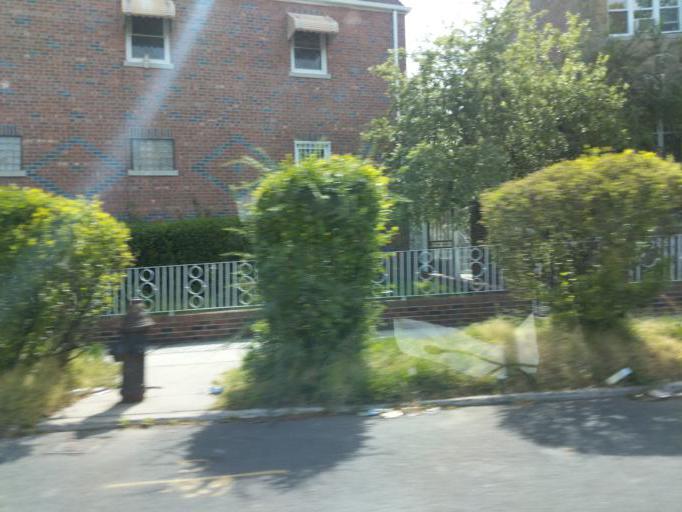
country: US
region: New York
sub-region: Kings County
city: Brooklyn
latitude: 40.6496
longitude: -73.9238
